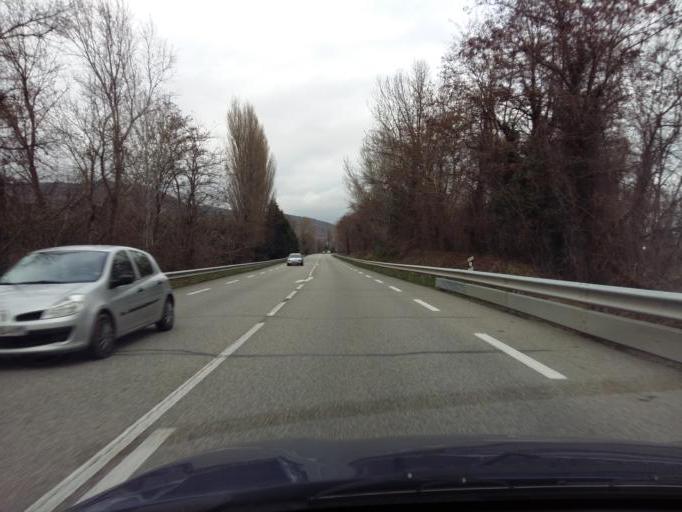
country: FR
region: Rhone-Alpes
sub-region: Departement de l'Ardeche
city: Beauchastel
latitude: 44.8153
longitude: 4.8053
